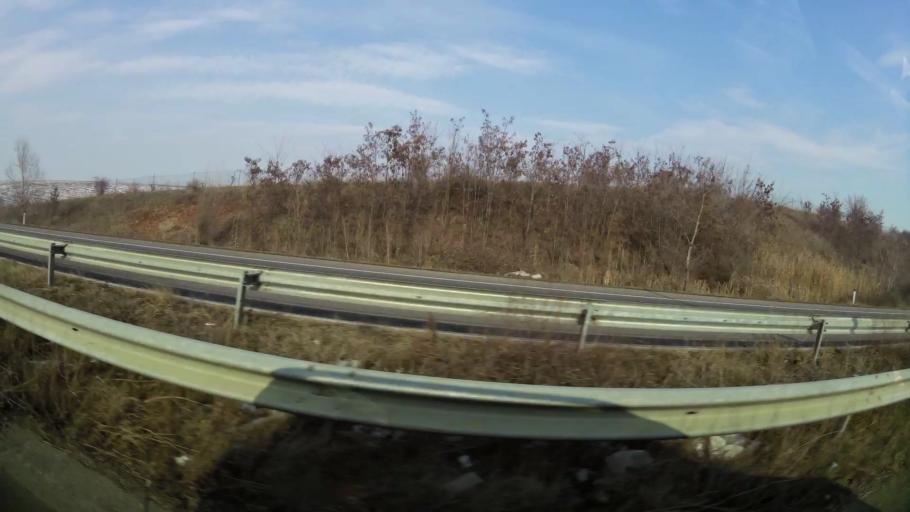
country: MK
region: Butel
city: Butel
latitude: 42.0328
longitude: 21.4764
